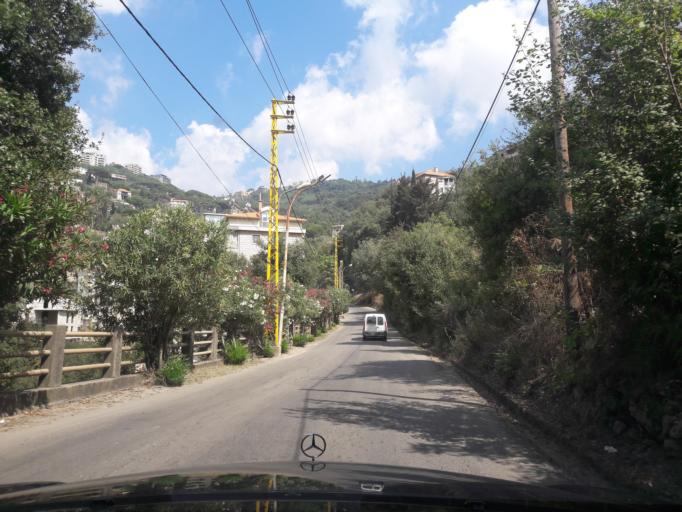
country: LB
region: Mont-Liban
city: Djounie
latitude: 33.9262
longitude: 35.6673
